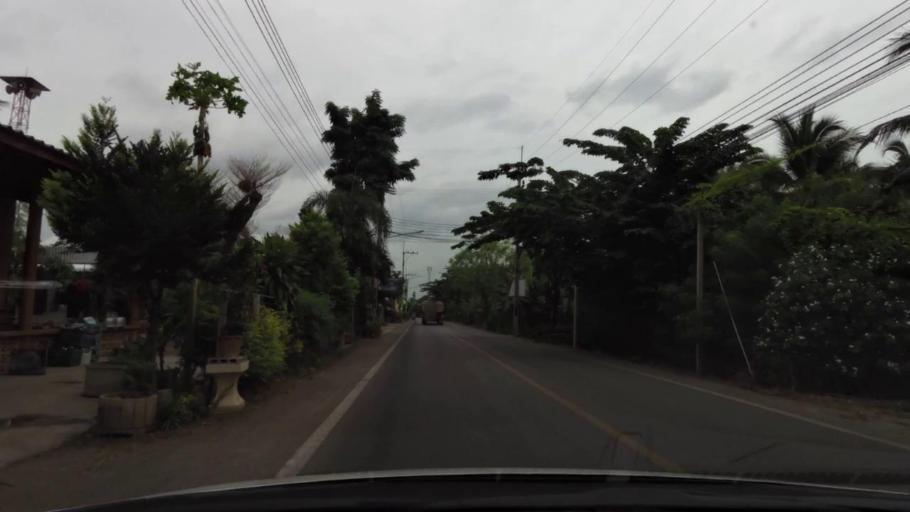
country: TH
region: Ratchaburi
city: Damnoen Saduak
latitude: 13.5712
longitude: 100.0060
